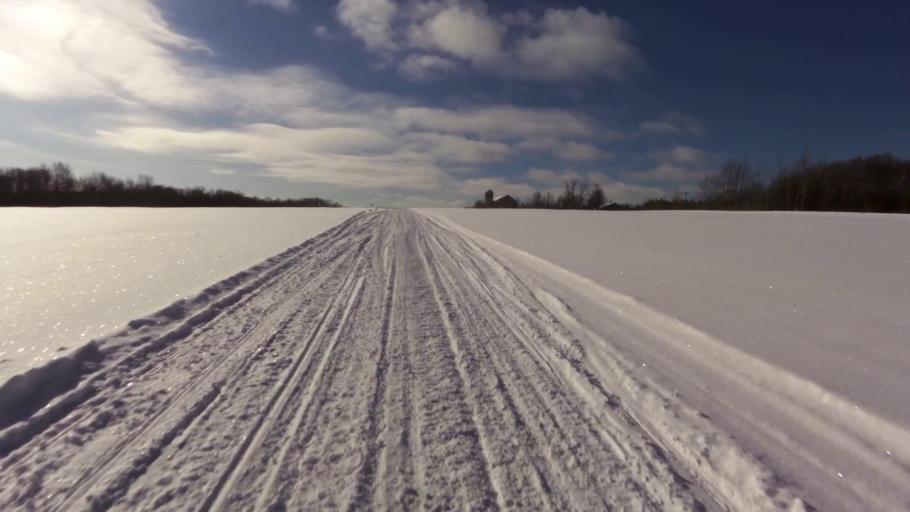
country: US
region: New York
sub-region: Chautauqua County
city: Falconer
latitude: 42.2691
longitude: -79.1134
